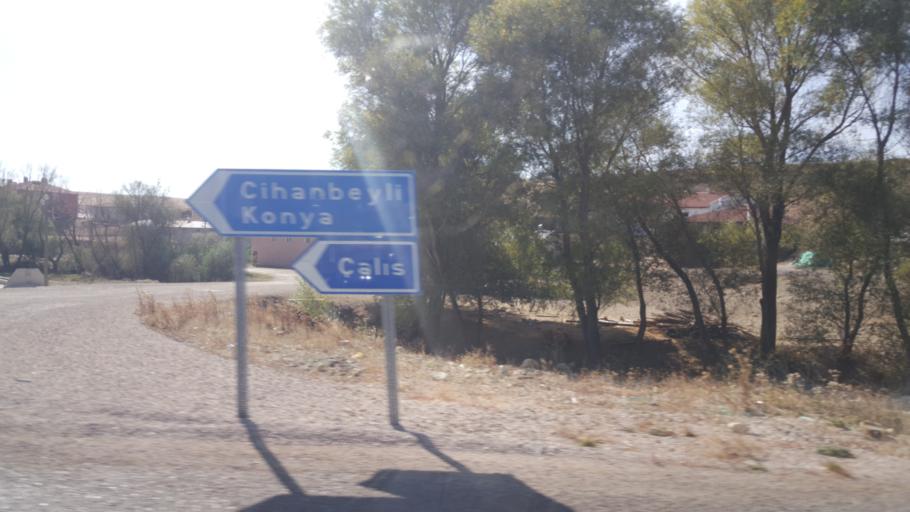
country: TR
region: Ankara
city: Haymana
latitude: 39.4192
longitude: 32.5944
